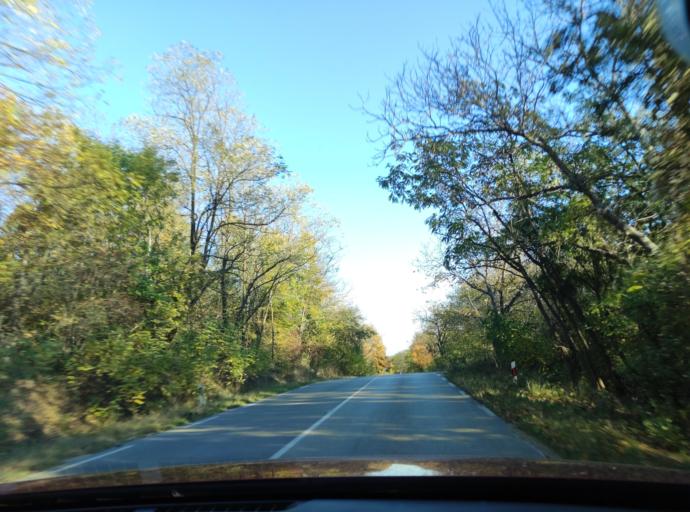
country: BG
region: Montana
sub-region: Obshtina Montana
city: Montana
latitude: 43.4063
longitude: 23.0655
